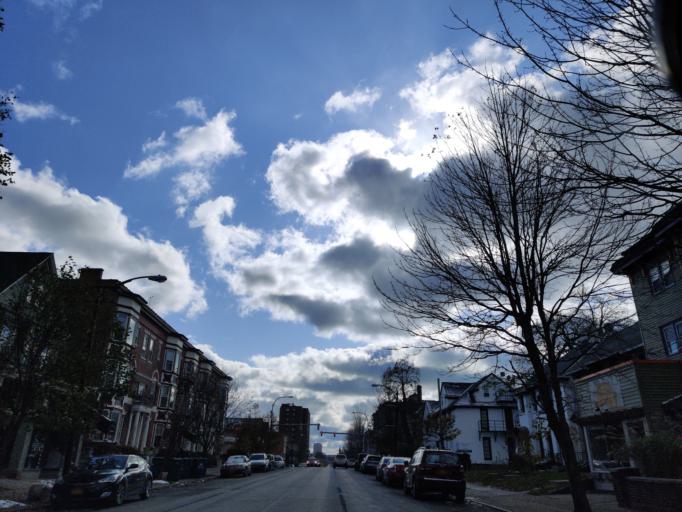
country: US
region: New York
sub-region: Erie County
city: Buffalo
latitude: 42.9140
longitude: -78.8771
